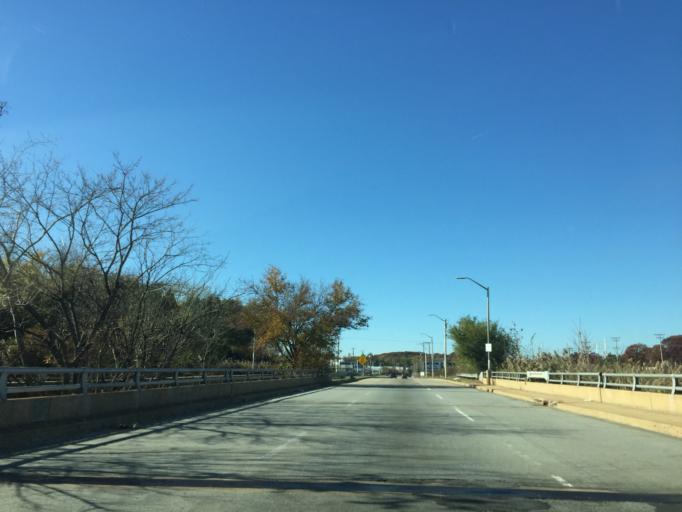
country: US
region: Maryland
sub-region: Anne Arundel County
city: Brooklyn Park
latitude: 39.2404
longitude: -76.6188
